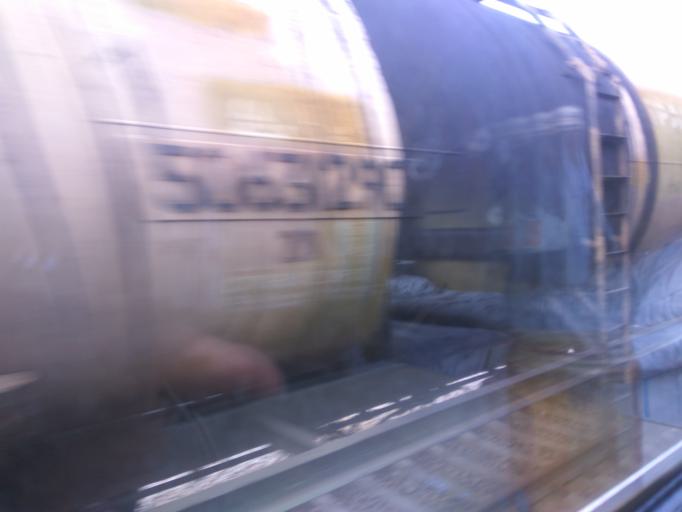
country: RU
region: Saratov
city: Rtishchevo
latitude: 52.2072
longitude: 43.8869
